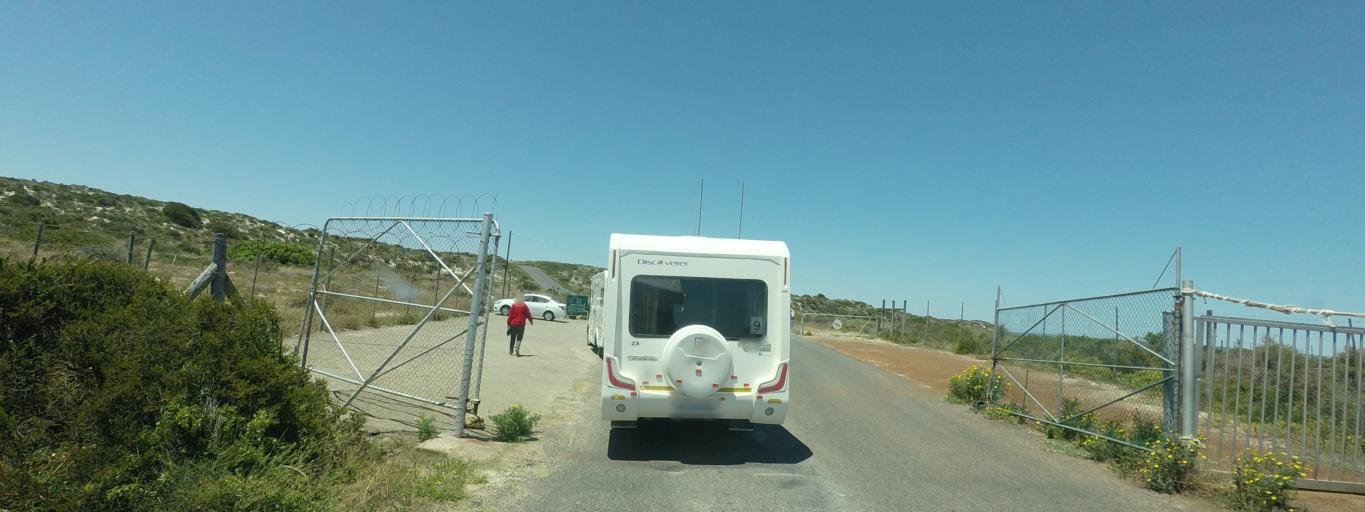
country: ZA
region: Western Cape
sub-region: West Coast District Municipality
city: Saldanha
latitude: -33.1175
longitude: 18.0548
